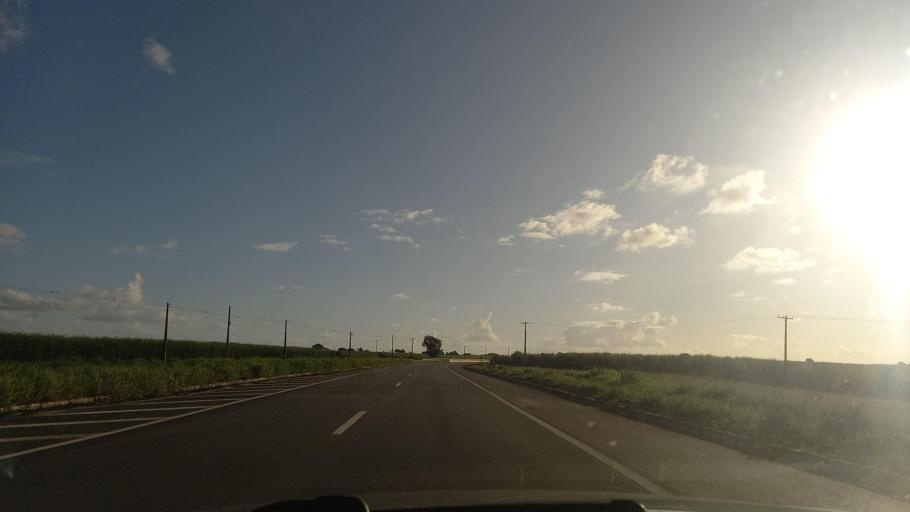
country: BR
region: Alagoas
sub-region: Campo Alegre
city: Campo Alegre
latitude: -9.8231
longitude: -36.2378
